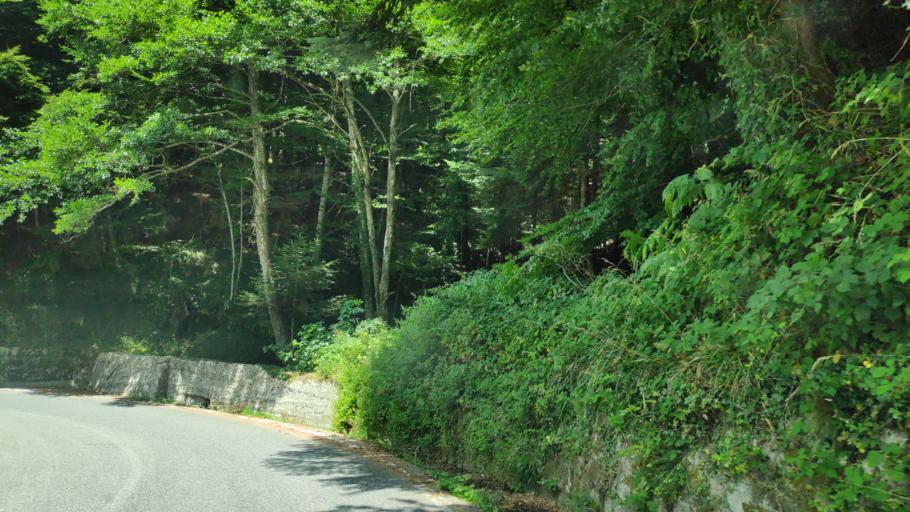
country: IT
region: Calabria
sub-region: Provincia di Vibo-Valentia
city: Mongiana
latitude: 38.5227
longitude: 16.3396
